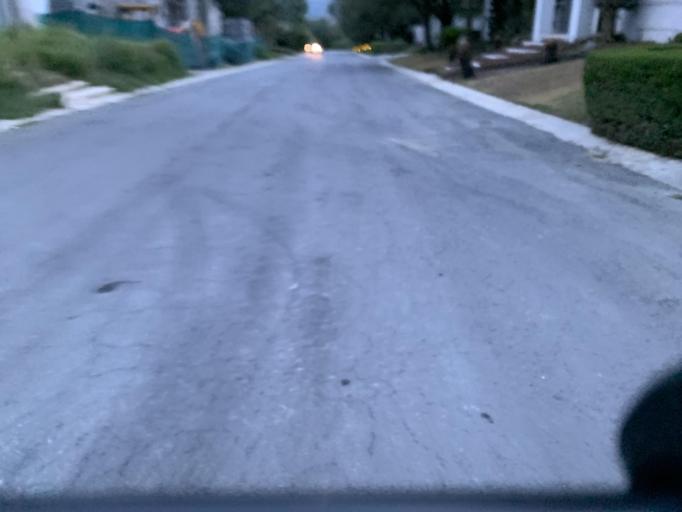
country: MX
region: Nuevo Leon
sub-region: Juarez
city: Bosques de San Pedro
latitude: 25.5120
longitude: -100.1855
